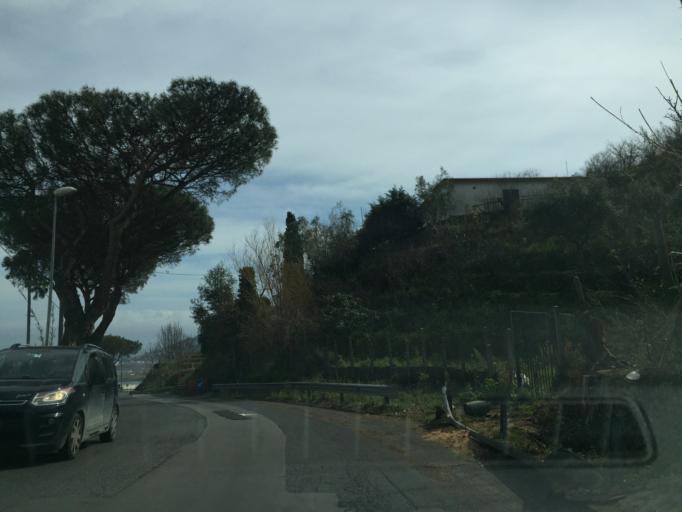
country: IT
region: Campania
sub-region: Provincia di Napoli
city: Monte di Procida
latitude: 40.7952
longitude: 14.0607
